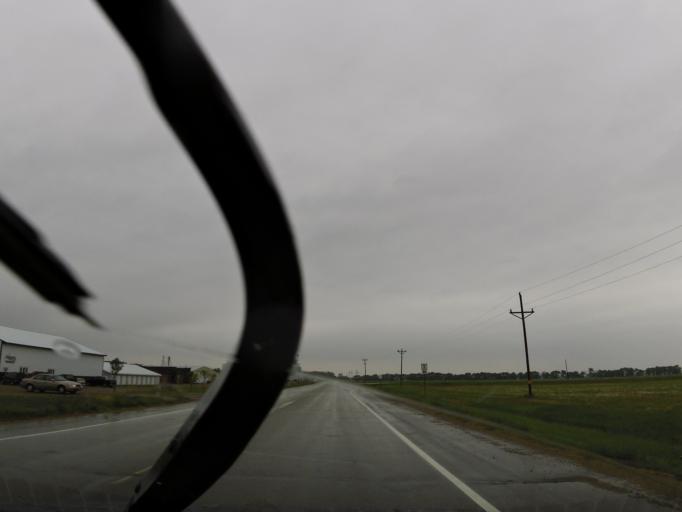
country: US
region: Minnesota
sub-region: Marshall County
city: Warren
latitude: 48.4545
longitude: -96.8693
